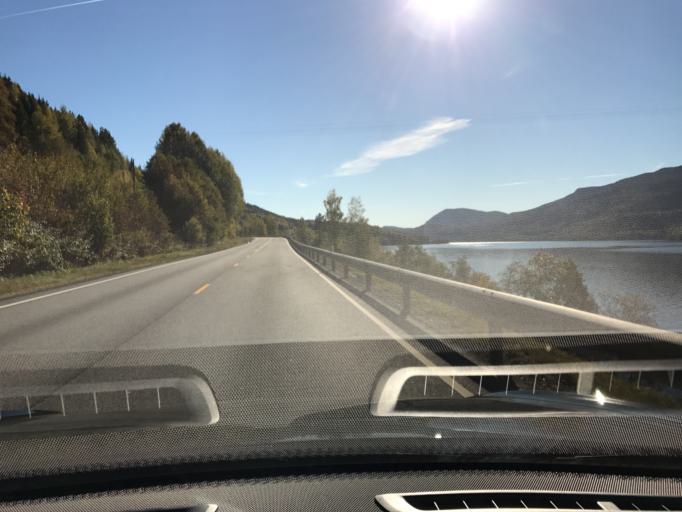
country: NO
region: Buskerud
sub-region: Krodsherad
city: Noresund
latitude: 60.3657
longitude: 9.6411
